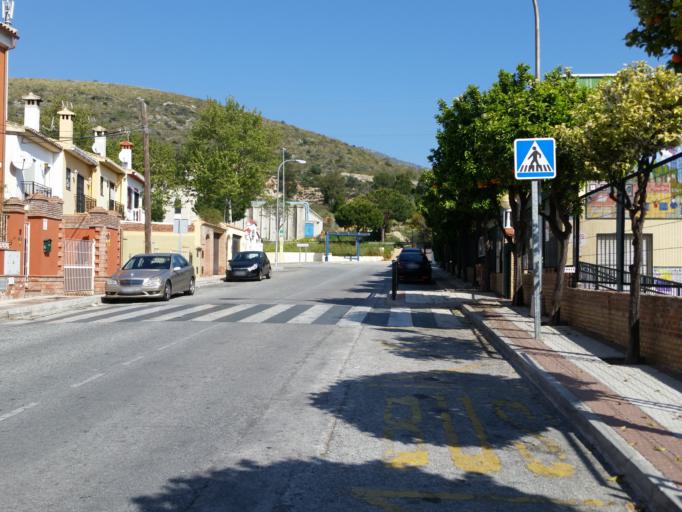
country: ES
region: Andalusia
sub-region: Provincia de Malaga
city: Benalmadena
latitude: 36.6086
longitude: -4.5362
